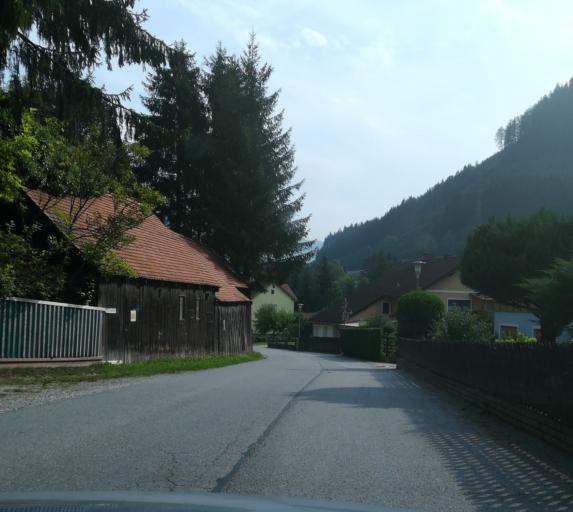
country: AT
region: Styria
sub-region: Politischer Bezirk Murtal
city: Sankt Georgen ob Judenburg
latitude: 47.2024
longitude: 14.4464
